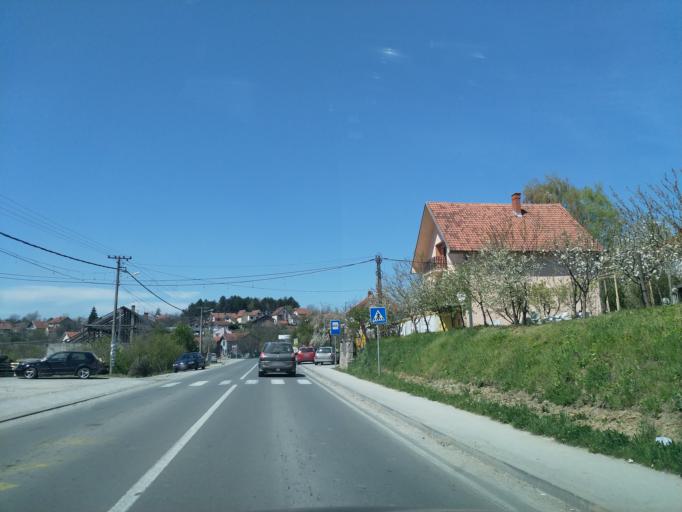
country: RS
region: Central Serbia
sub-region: Sumadijski Okrug
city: Arangelovac
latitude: 44.3280
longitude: 20.5214
